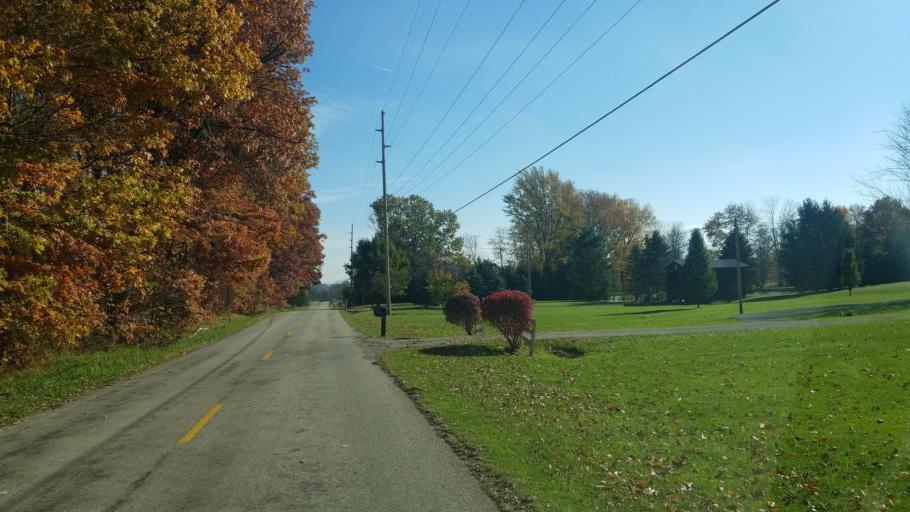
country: US
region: Ohio
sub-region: Ashland County
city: Ashland
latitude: 40.8289
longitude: -82.3317
